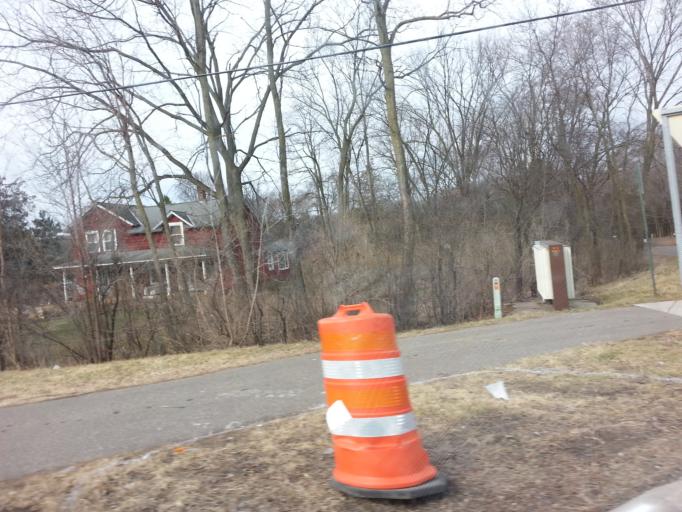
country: US
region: Minnesota
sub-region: Washington County
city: Lakeland
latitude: 44.9495
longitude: -92.7712
